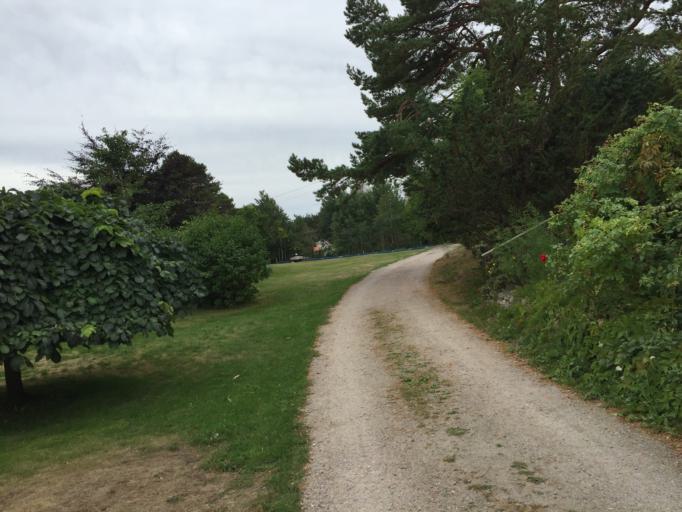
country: NO
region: Ostfold
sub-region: Hvaler
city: Skjaerhalden
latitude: 59.0325
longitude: 11.0561
